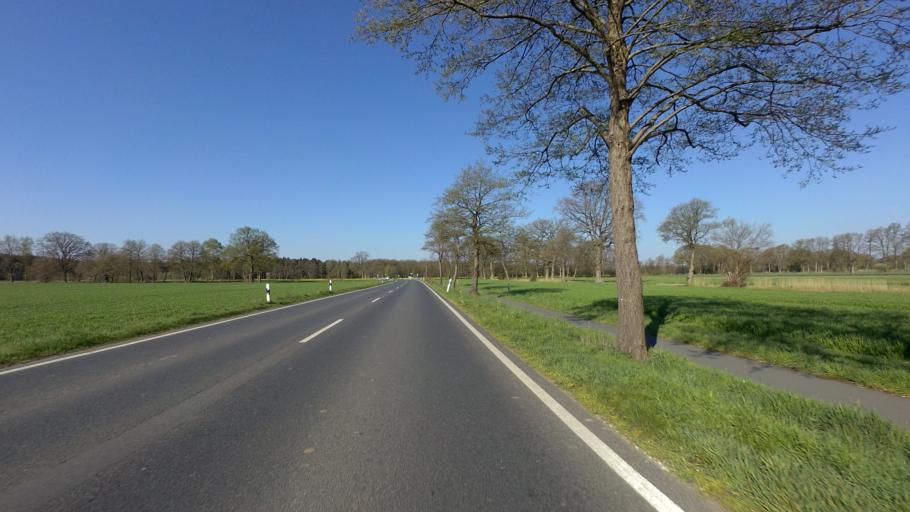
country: DE
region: Lower Saxony
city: Hemsbunde
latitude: 53.1252
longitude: 9.4527
